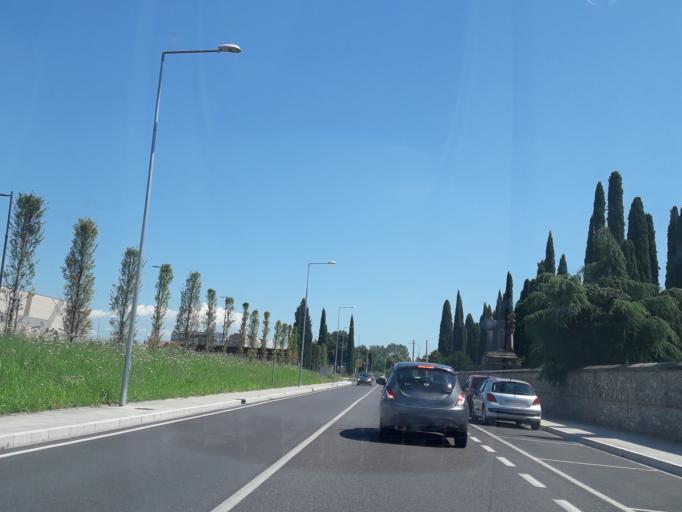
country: IT
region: Friuli Venezia Giulia
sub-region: Provincia di Udine
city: Udine
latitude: 46.0638
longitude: 13.2169
